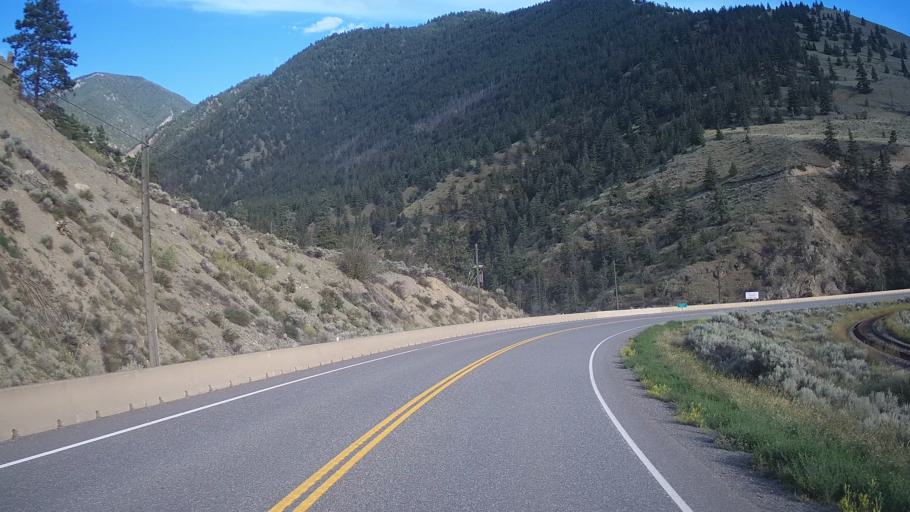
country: CA
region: British Columbia
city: Lillooet
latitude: 50.7941
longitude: -121.8390
